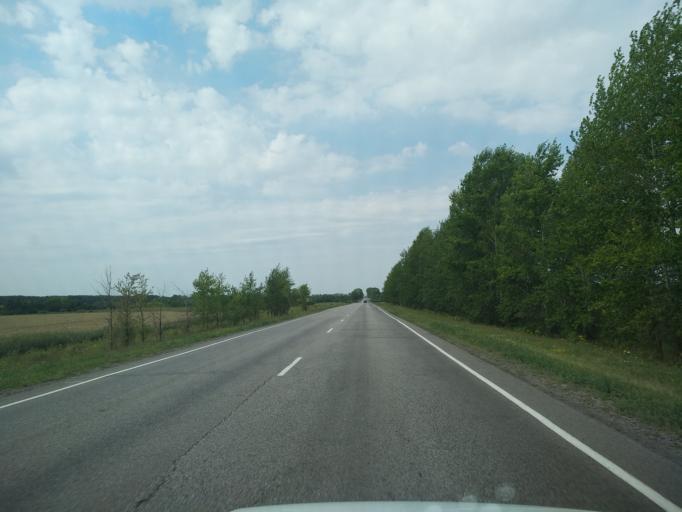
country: RU
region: Voronezj
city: Pereleshino
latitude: 51.7158
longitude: 40.0142
